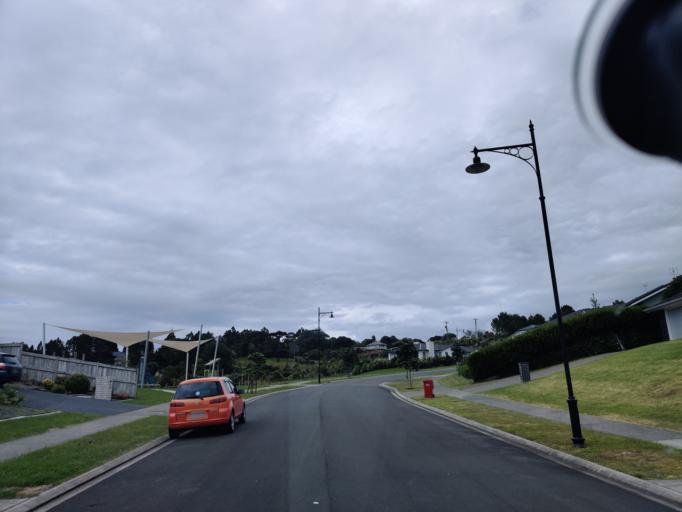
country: NZ
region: Auckland
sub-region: Auckland
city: Rothesay Bay
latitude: -36.5697
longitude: 174.6860
